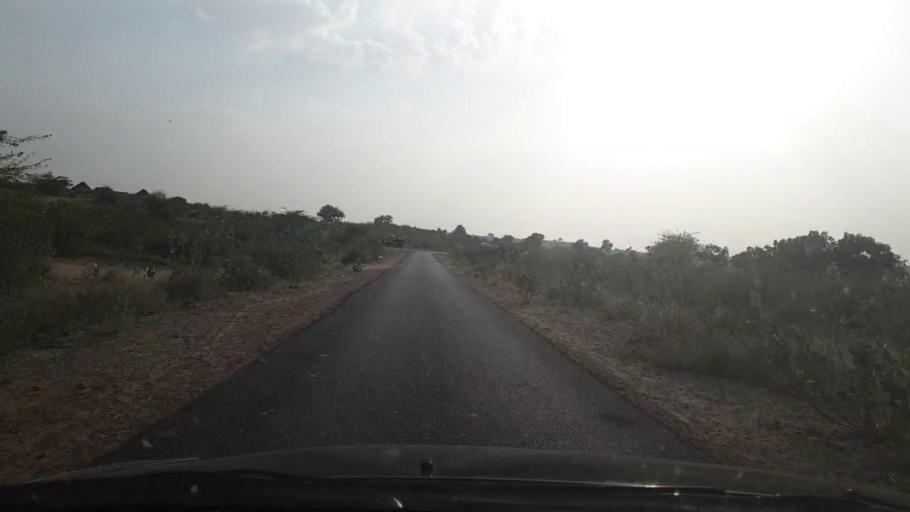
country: PK
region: Sindh
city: Islamkot
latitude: 25.0594
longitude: 70.4560
